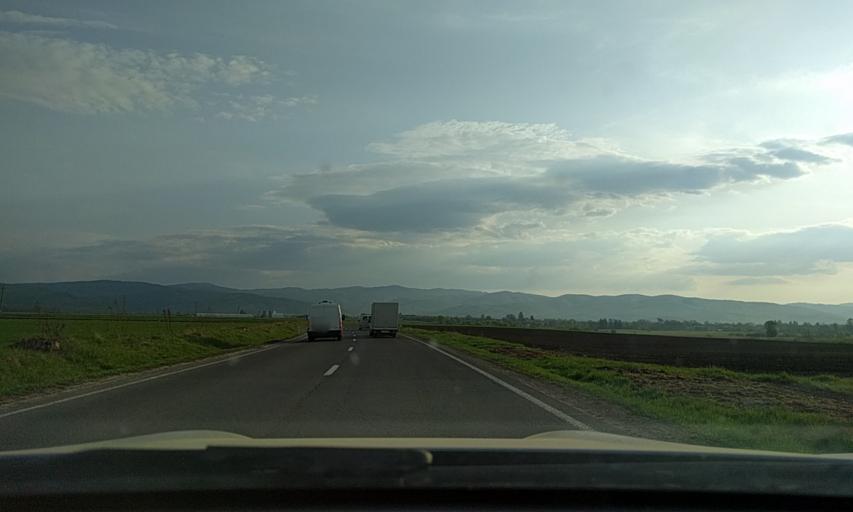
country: RO
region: Covasna
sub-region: Comuna Lemnia
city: Lemnia
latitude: 46.0385
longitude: 26.2468
